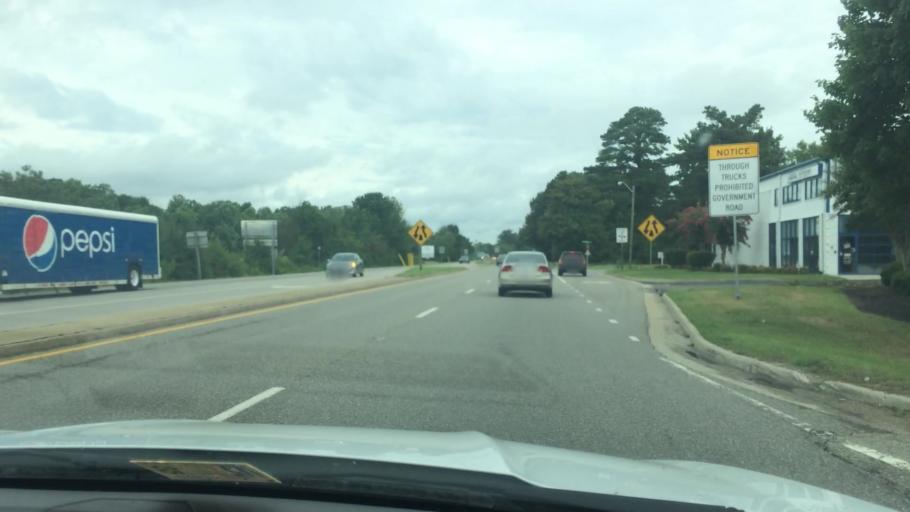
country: US
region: Virginia
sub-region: City of Williamsburg
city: Williamsburg
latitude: 37.2530
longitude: -76.6633
